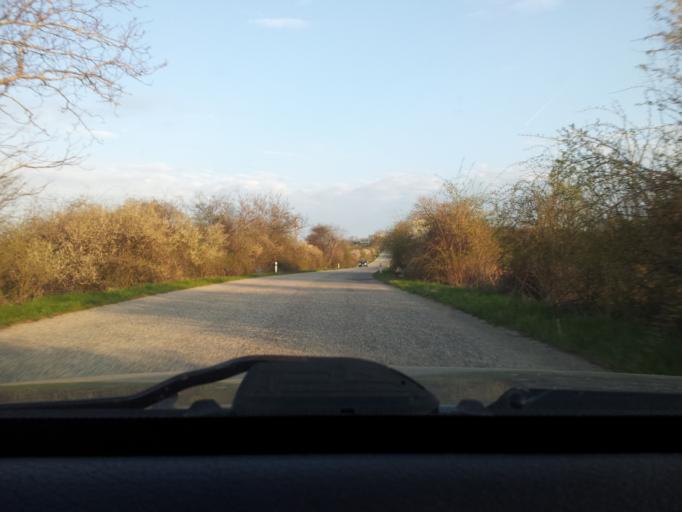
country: SK
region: Nitriansky
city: Tlmace
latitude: 48.2851
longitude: 18.4619
